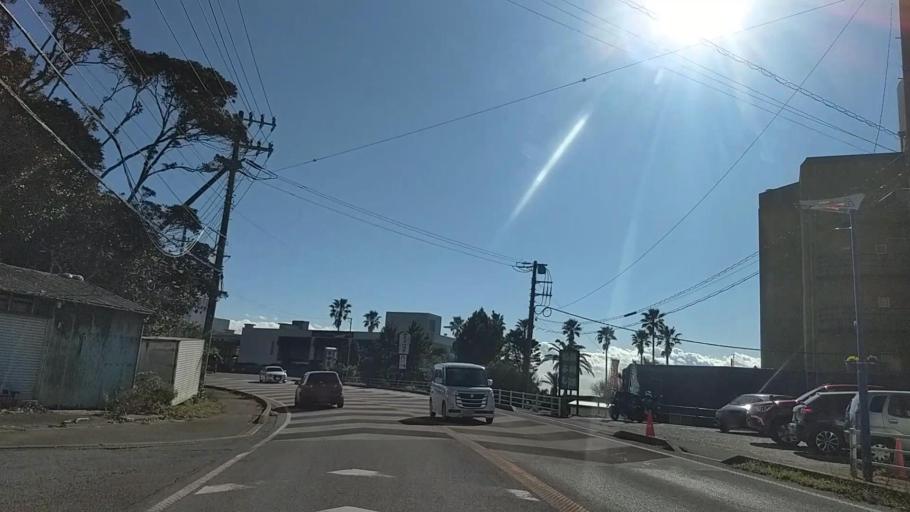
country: JP
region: Chiba
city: Kawaguchi
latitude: 35.1217
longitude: 140.1729
